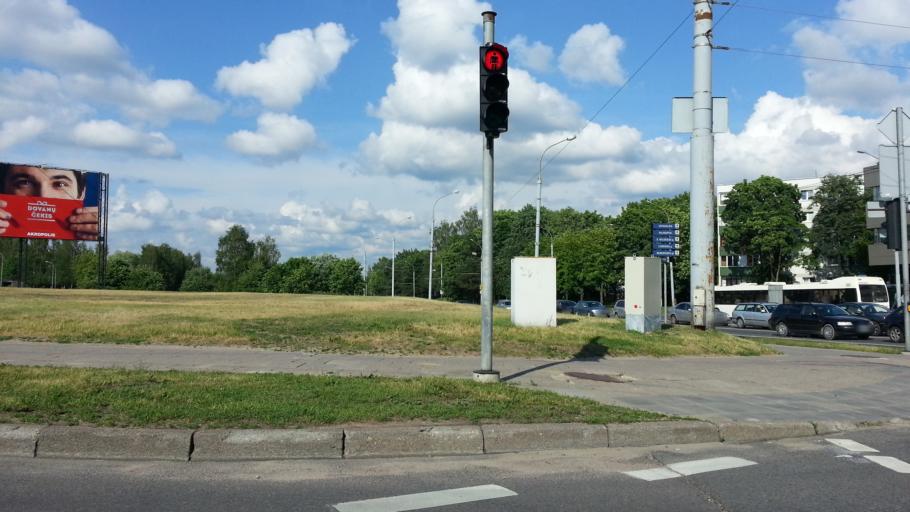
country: LT
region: Vilnius County
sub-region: Vilnius
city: Vilnius
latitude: 54.7206
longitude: 25.3023
